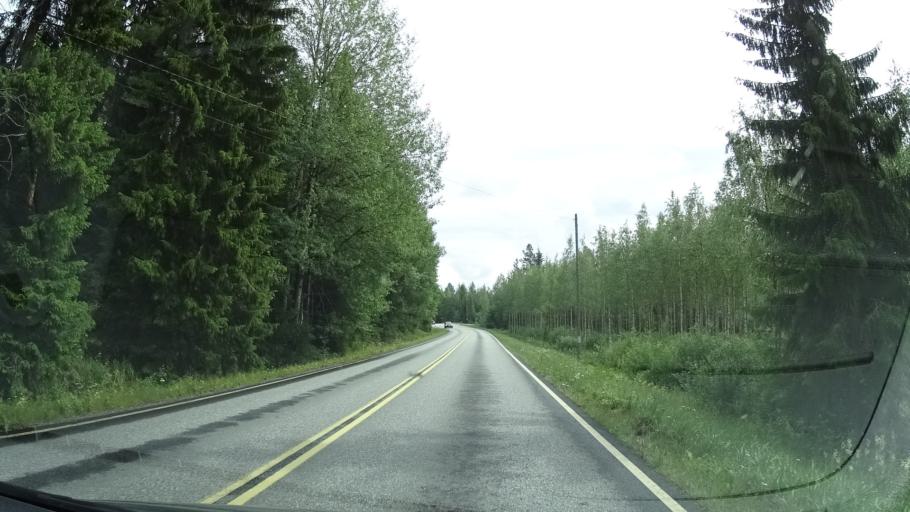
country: FI
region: Pirkanmaa
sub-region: Etelae-Pirkanmaa
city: Urjala
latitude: 61.0854
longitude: 23.4019
